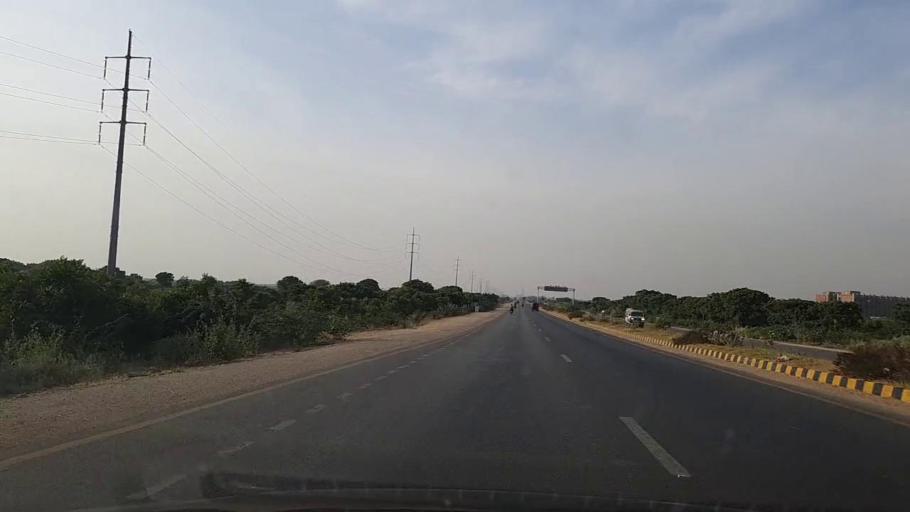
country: PK
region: Sindh
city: Gharo
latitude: 24.7692
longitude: 67.5487
